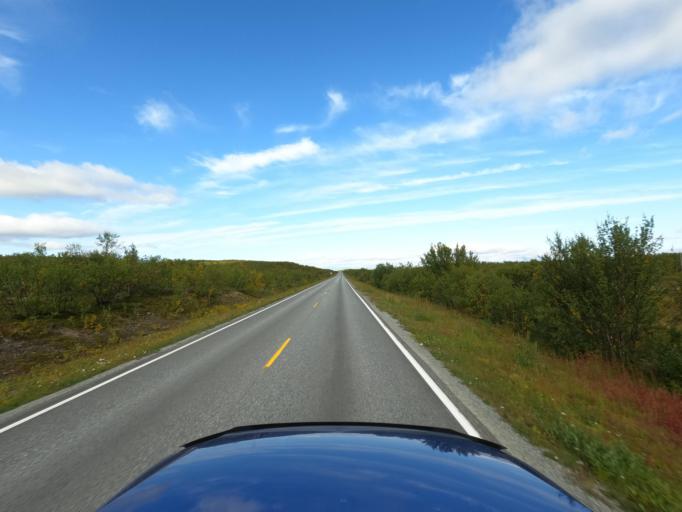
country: NO
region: Finnmark Fylke
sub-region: Karasjok
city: Karasjohka
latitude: 69.6802
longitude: 25.2630
